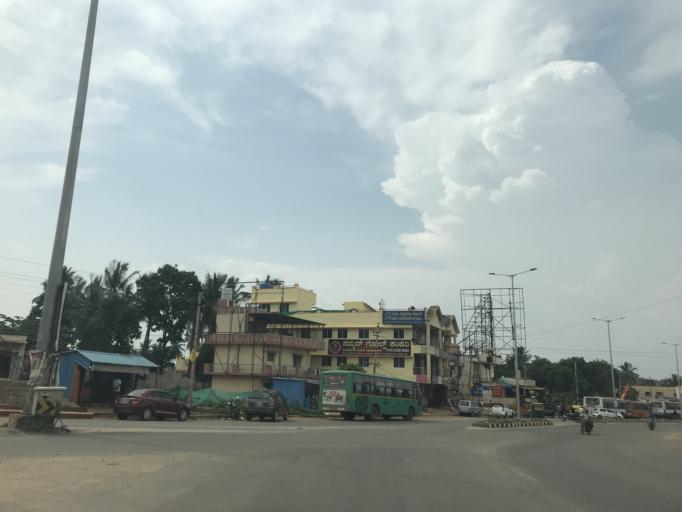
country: IN
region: Karnataka
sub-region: Bangalore Urban
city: Yelahanka
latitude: 13.1332
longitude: 77.6668
